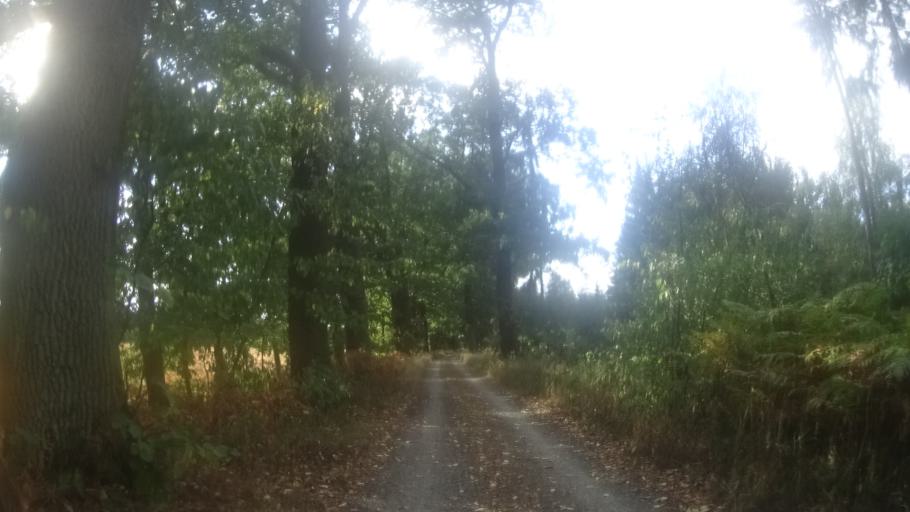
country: CZ
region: Kralovehradecky
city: Trebechovice pod Orebem
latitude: 50.1797
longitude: 16.0270
